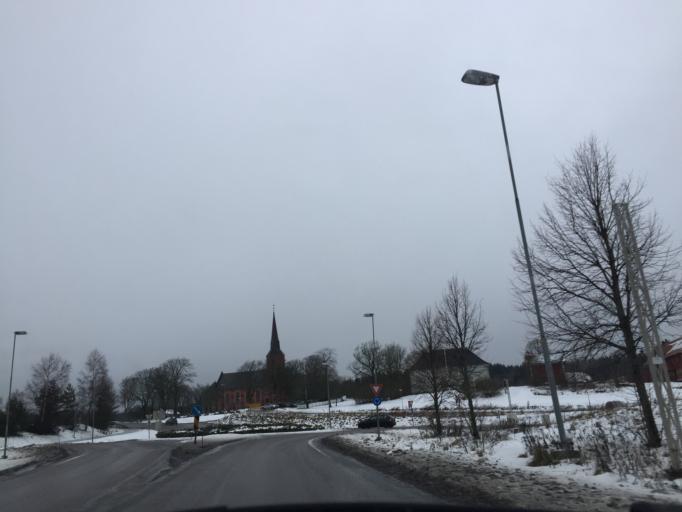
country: NO
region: Akershus
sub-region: Vestby
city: Vestby
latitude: 59.6024
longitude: 10.7365
